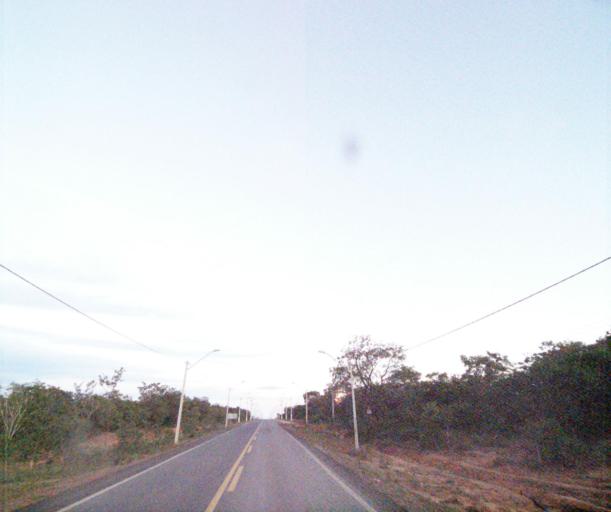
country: BR
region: Bahia
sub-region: Correntina
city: Correntina
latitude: -13.8190
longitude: -44.4792
